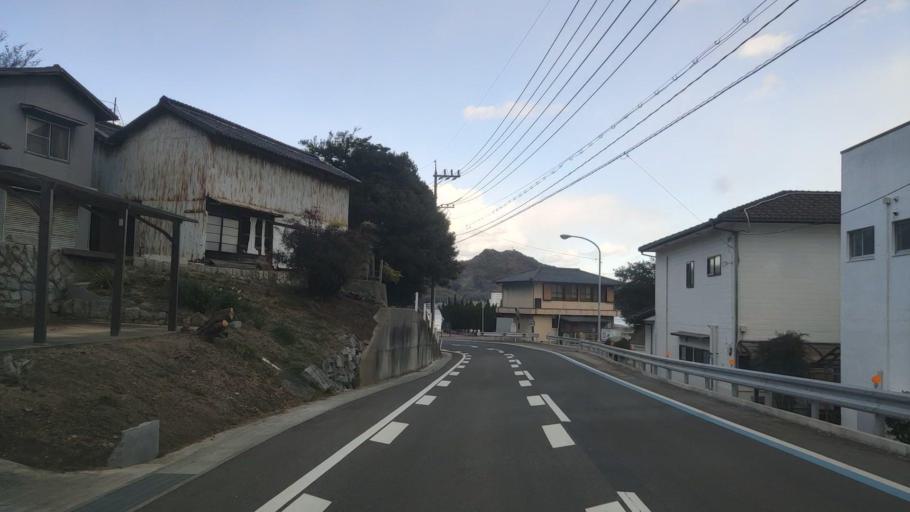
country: JP
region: Hiroshima
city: Innoshima
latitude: 34.1992
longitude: 133.0889
